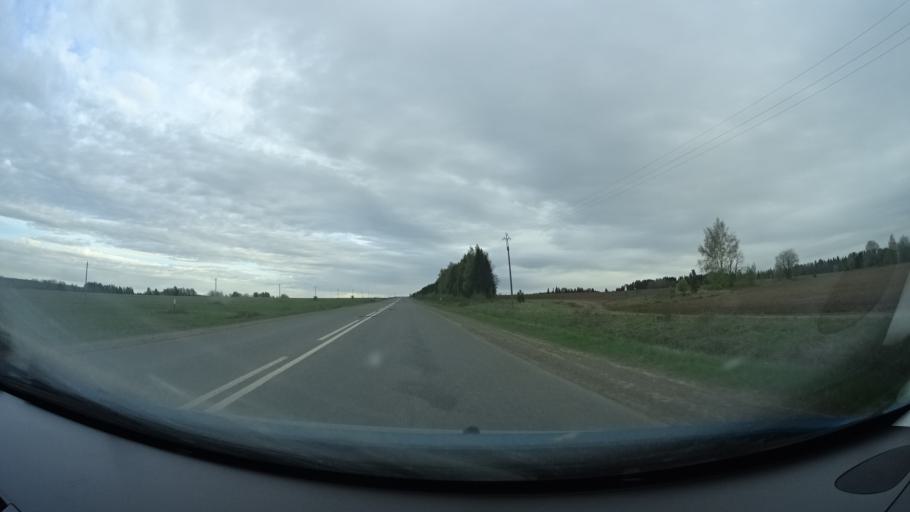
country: RU
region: Perm
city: Osa
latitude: 57.2783
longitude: 55.5668
